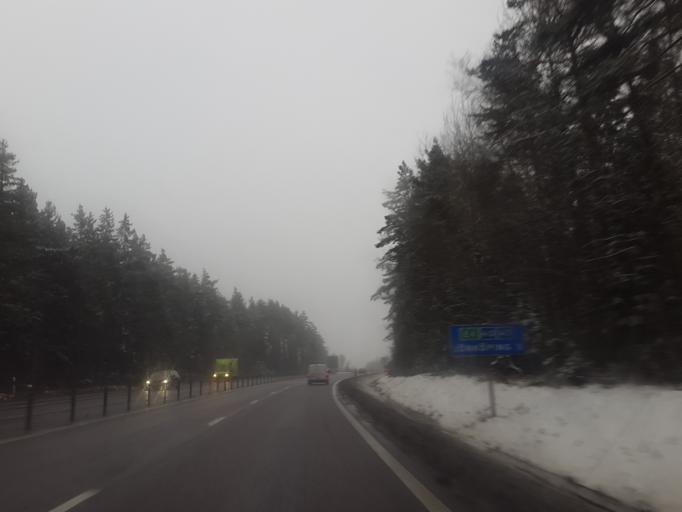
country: SE
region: Joenkoeping
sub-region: Jonkopings Kommun
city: Jonkoping
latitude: 57.7601
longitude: 14.1055
